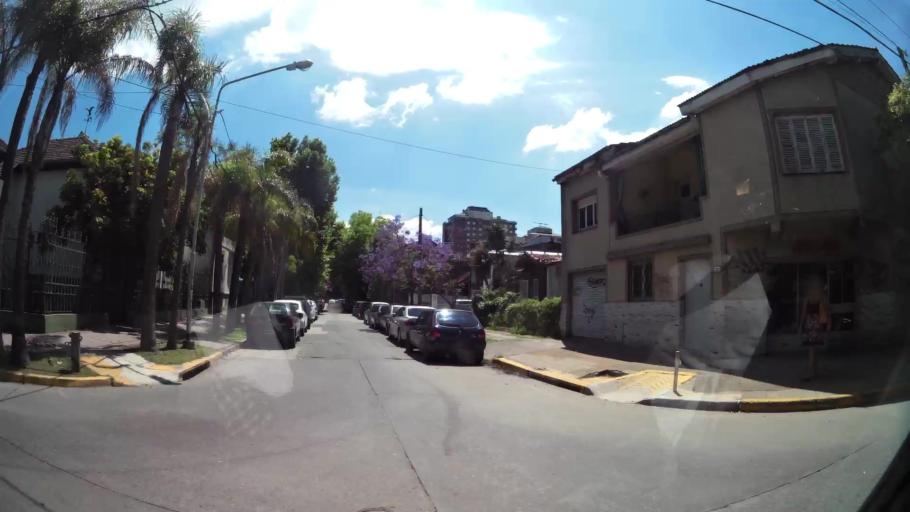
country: AR
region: Buenos Aires
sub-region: Partido de Tigre
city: Tigre
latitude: -34.4262
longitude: -58.5782
